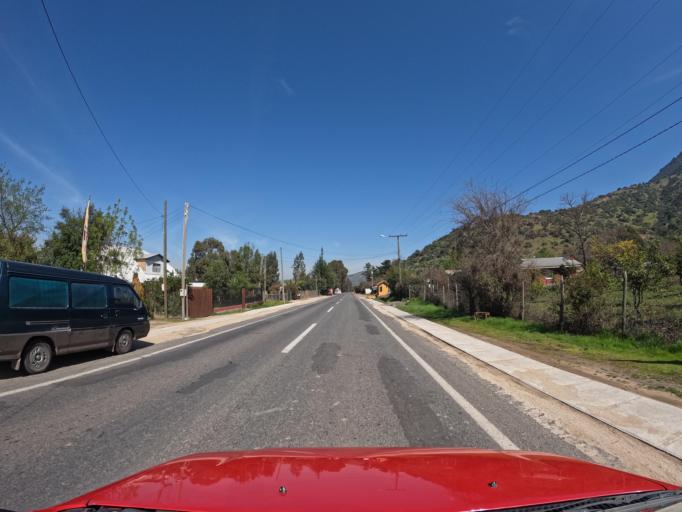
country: CL
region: Maule
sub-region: Provincia de Curico
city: Rauco
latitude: -35.0508
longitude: -71.6013
